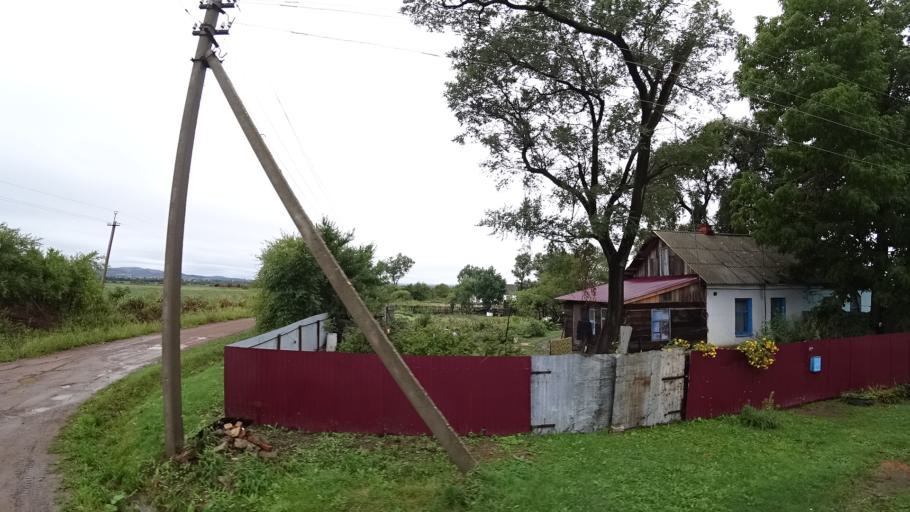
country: RU
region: Primorskiy
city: Monastyrishche
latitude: 44.2342
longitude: 132.4648
